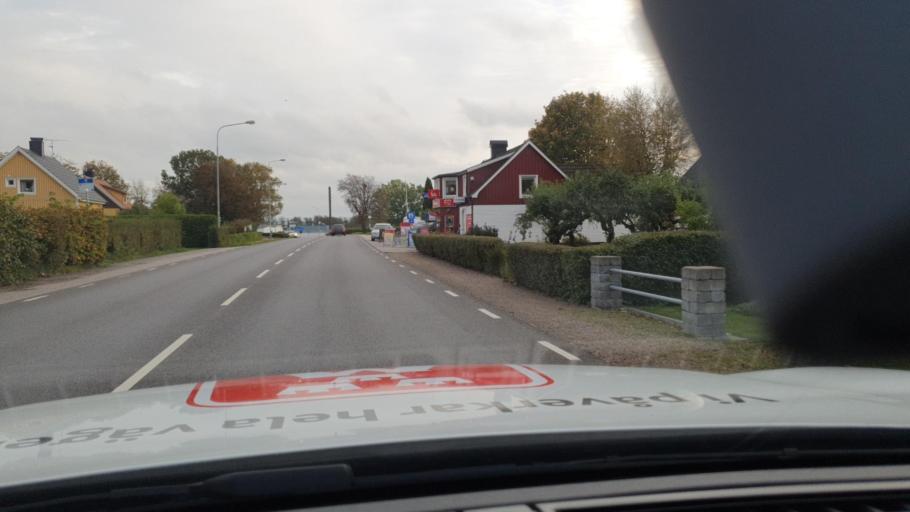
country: SE
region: Halland
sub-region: Laholms Kommun
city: Laholm
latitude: 56.5276
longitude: 13.0523
